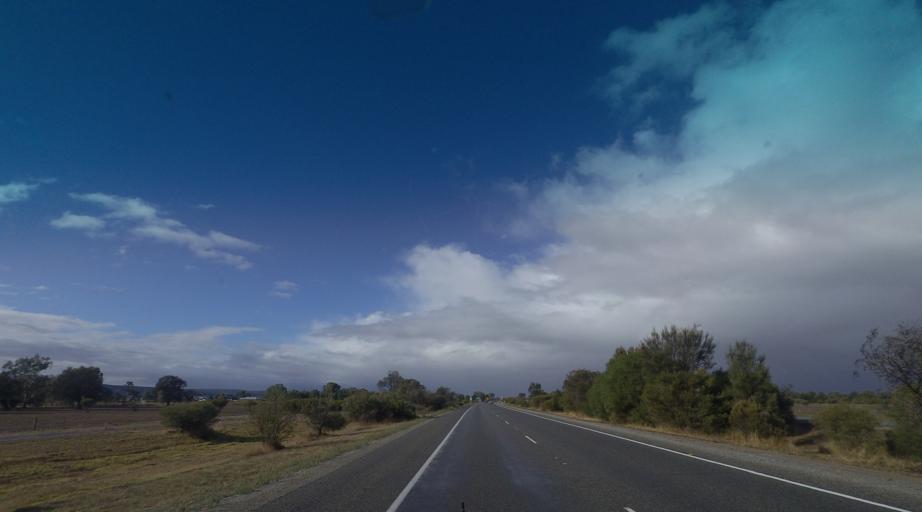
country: AU
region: Western Australia
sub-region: Serpentine-Jarrahdale
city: Oakford
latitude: -32.1753
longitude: 115.9614
